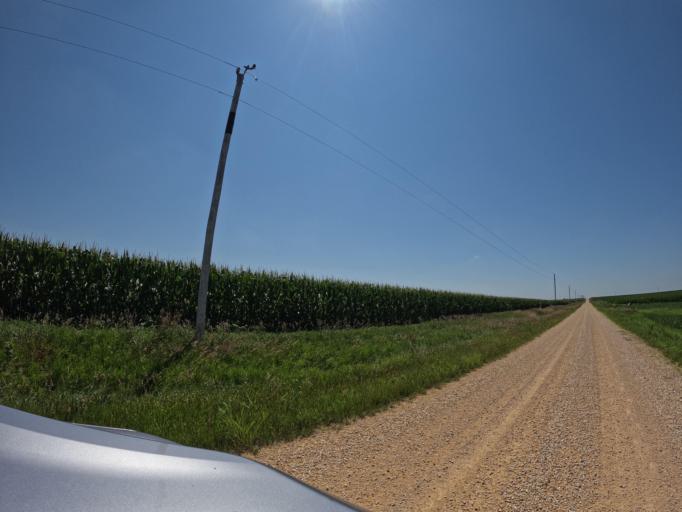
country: US
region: Iowa
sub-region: Clinton County
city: Camanche
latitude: 41.7913
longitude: -90.3937
